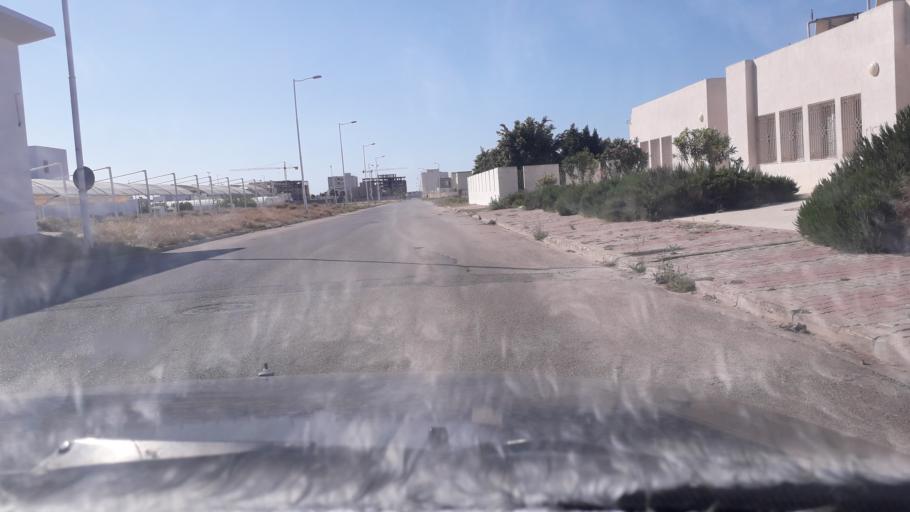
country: TN
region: Safaqis
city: Al Qarmadah
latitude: 34.8379
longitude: 10.7547
